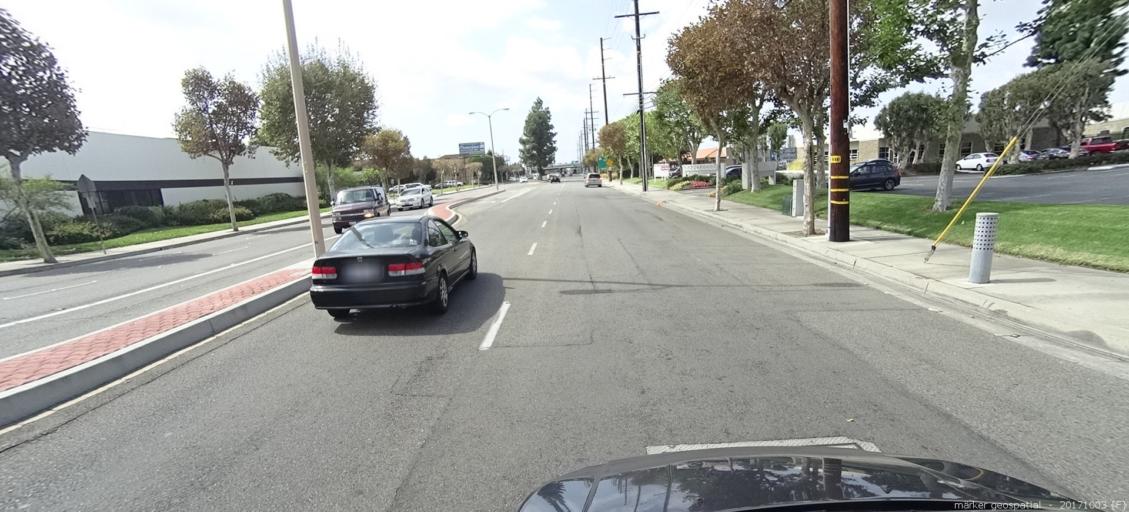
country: US
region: California
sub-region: Orange County
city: Garden Grove
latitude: 33.7745
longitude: -117.8996
